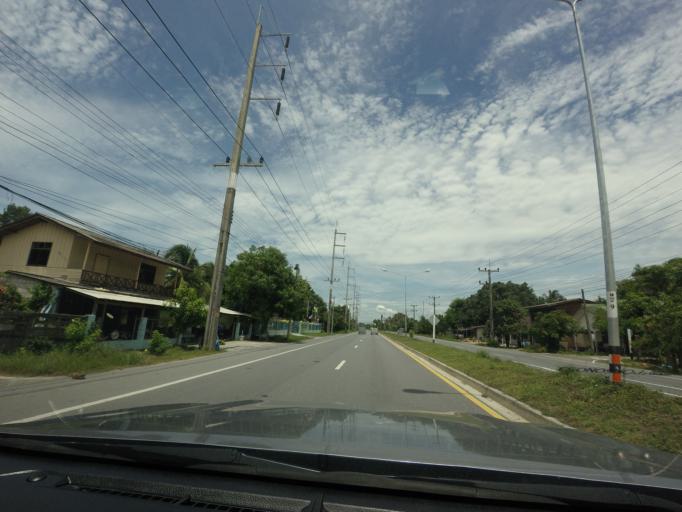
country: TH
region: Songkhla
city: Krasae Sin
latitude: 7.5828
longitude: 100.4067
